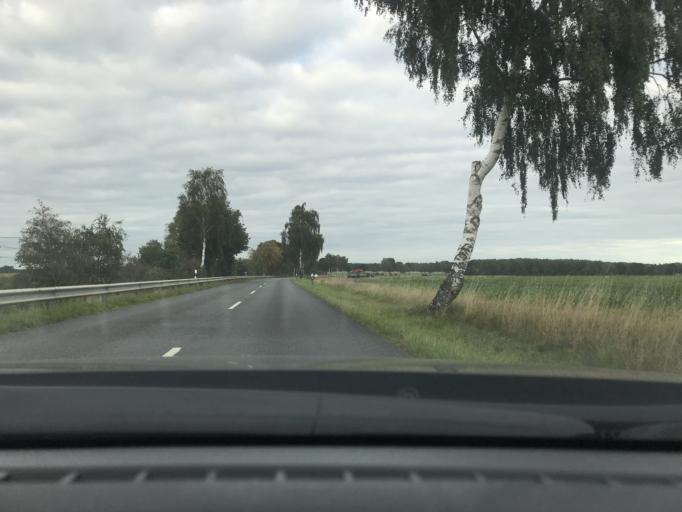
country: DE
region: Lower Saxony
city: Suderburg
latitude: 52.9085
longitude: 10.4376
